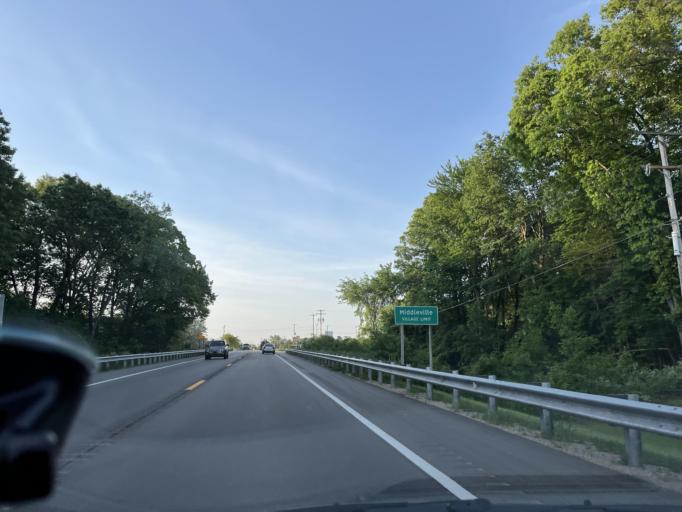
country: US
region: Michigan
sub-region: Barry County
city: Middleville
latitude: 42.7221
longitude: -85.4738
